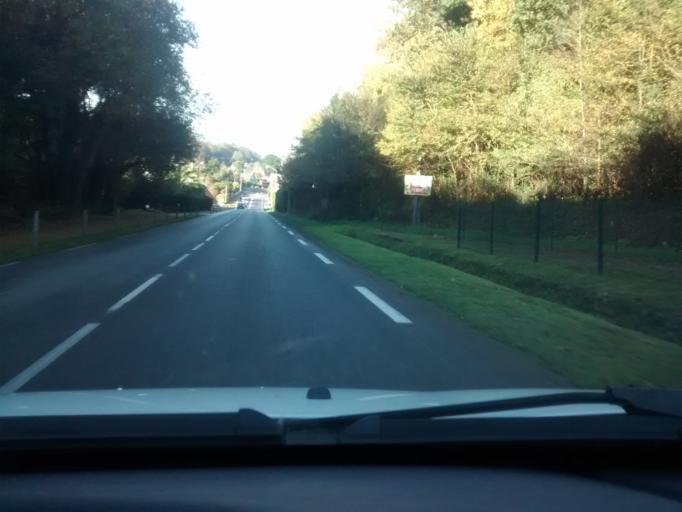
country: FR
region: Brittany
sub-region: Departement des Cotes-d'Armor
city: Louannec
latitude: 48.7959
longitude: -3.4216
